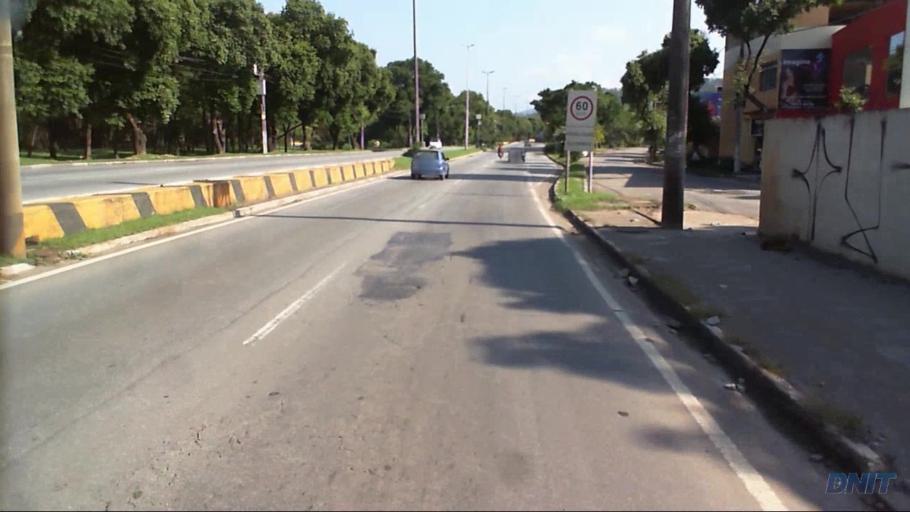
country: BR
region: Minas Gerais
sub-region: Ipatinga
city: Ipatinga
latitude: -19.5038
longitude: -42.5682
